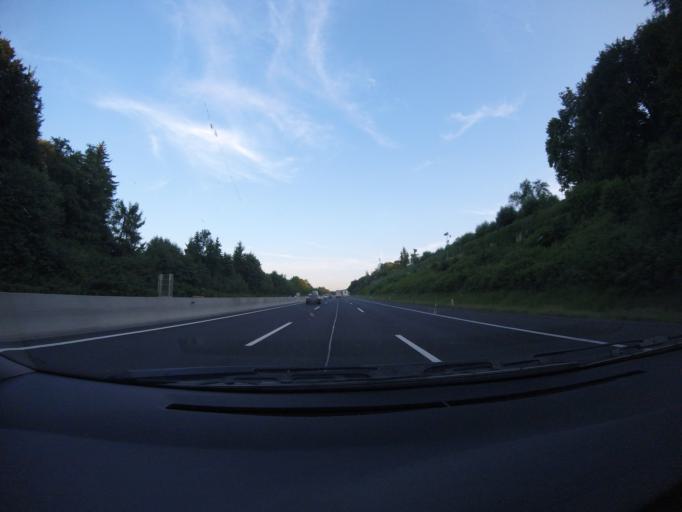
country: AT
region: Styria
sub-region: Politischer Bezirk Hartberg-Fuerstenfeld
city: Bad Waltersdorf
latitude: 47.1713
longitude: 15.9975
